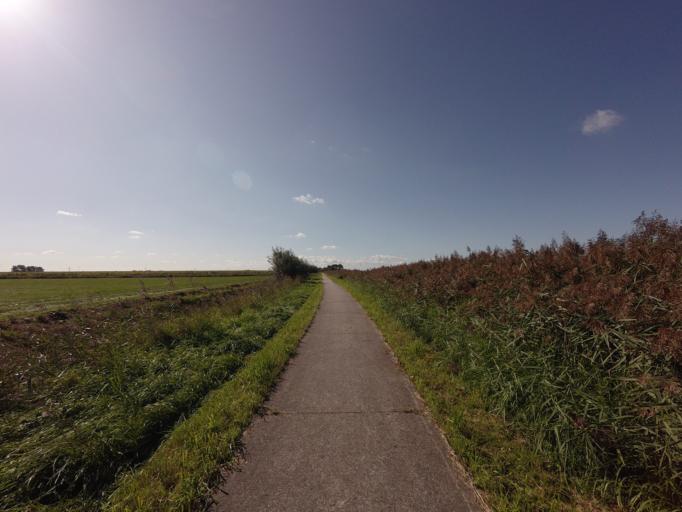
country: NL
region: Friesland
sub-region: Gemeente Boarnsterhim
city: Reduzum
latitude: 53.1338
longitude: 5.7577
